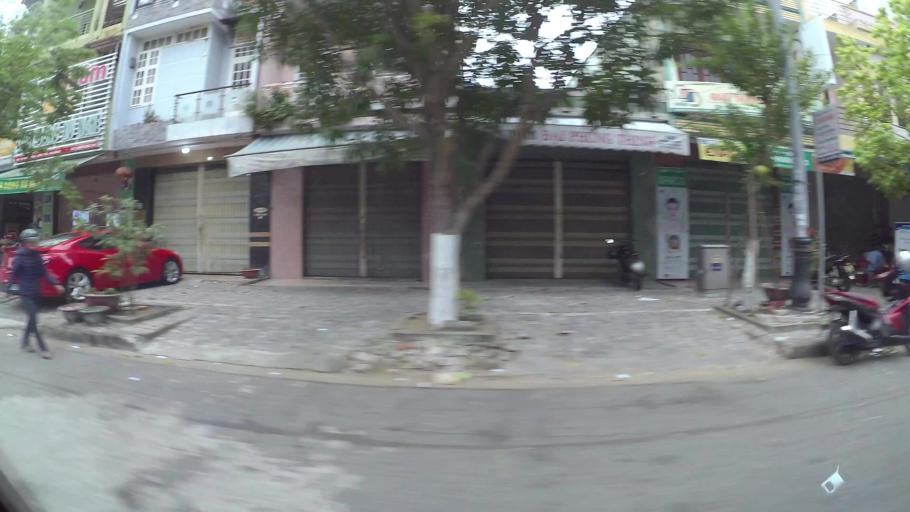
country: VN
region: Da Nang
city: Da Nang
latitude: 16.0875
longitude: 108.2384
